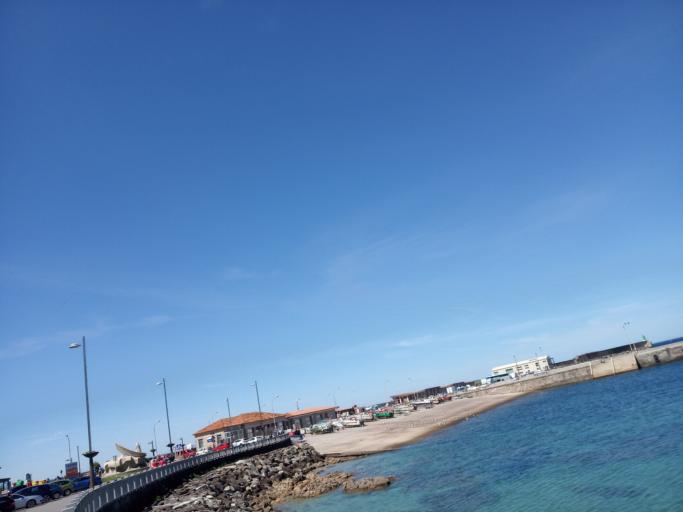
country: ES
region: Galicia
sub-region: Provincia de Pontevedra
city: A Guarda
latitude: 41.8987
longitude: -8.8749
